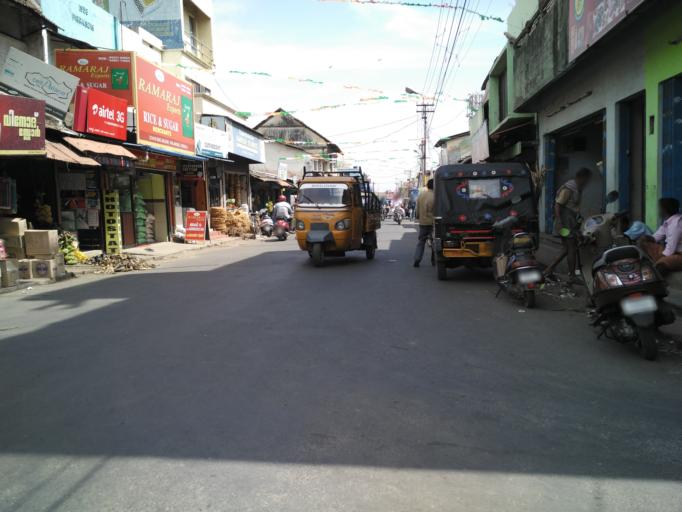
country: IN
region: Kerala
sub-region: Palakkad district
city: Palakkad
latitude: 10.7737
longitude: 76.6461
